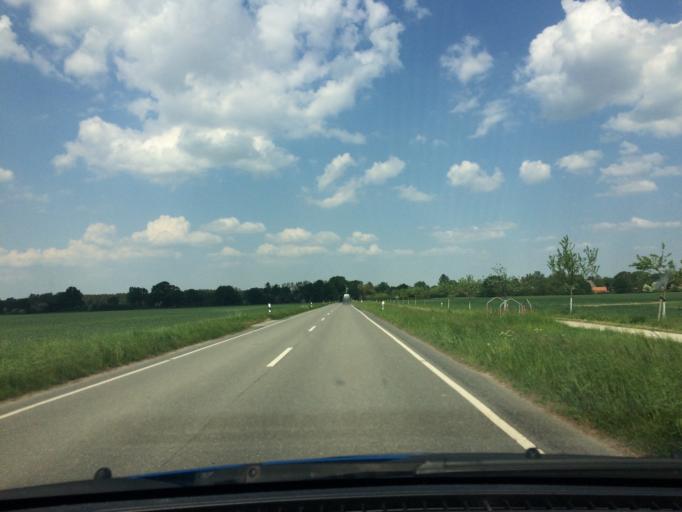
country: DE
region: Lower Saxony
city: Neu Darchau
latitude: 53.2548
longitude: 10.9113
